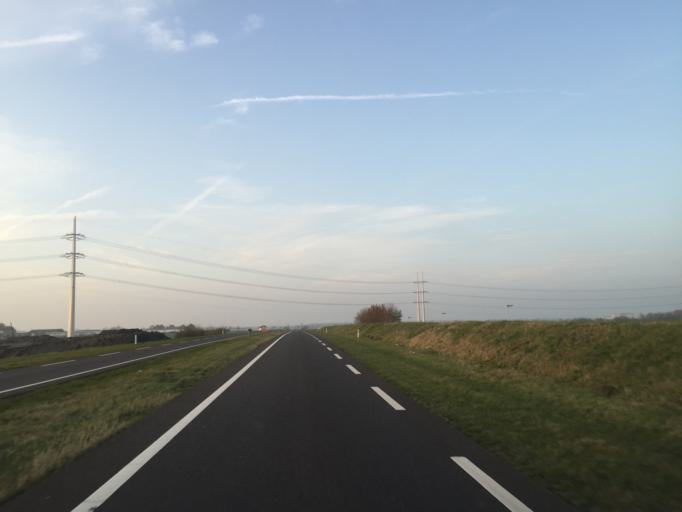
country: NL
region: South Holland
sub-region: Gemeente Lansingerland
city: Berkel en Rodenrijs
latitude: 52.0243
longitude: 4.4744
